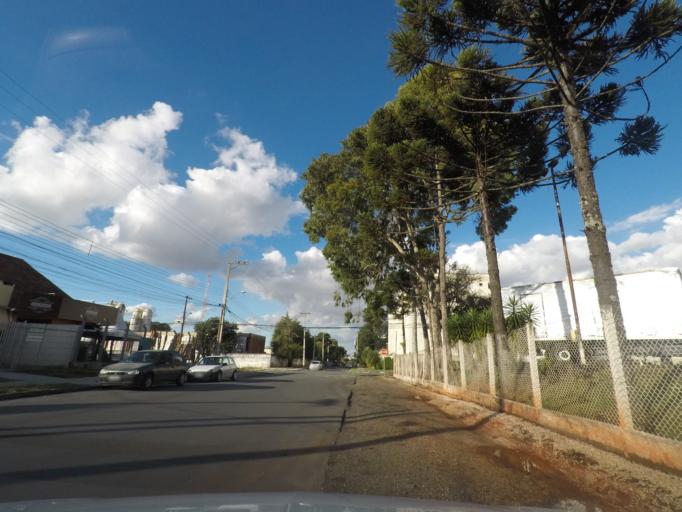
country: BR
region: Parana
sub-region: Curitiba
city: Curitiba
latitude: -25.4830
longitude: -49.2624
